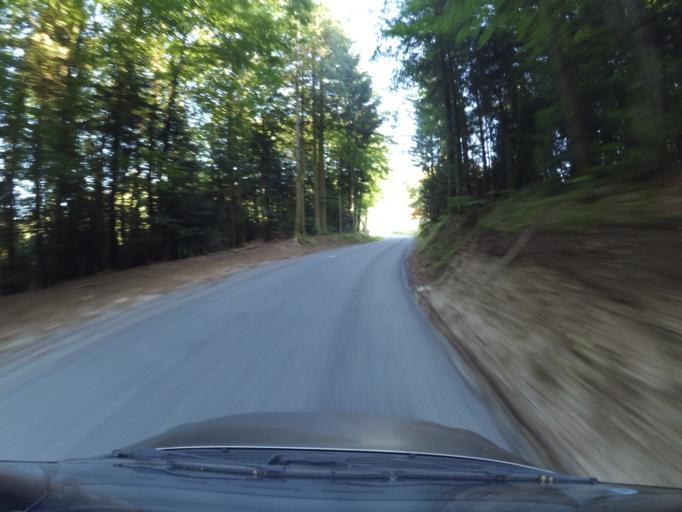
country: FR
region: Limousin
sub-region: Departement de la Creuse
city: Banize
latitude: 45.7832
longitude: 1.9889
